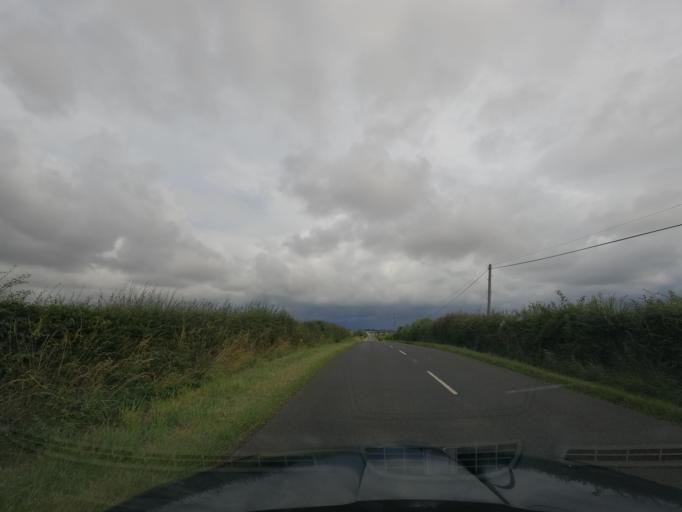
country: GB
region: England
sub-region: Northumberland
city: Ancroft
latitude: 55.6915
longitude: -2.0003
